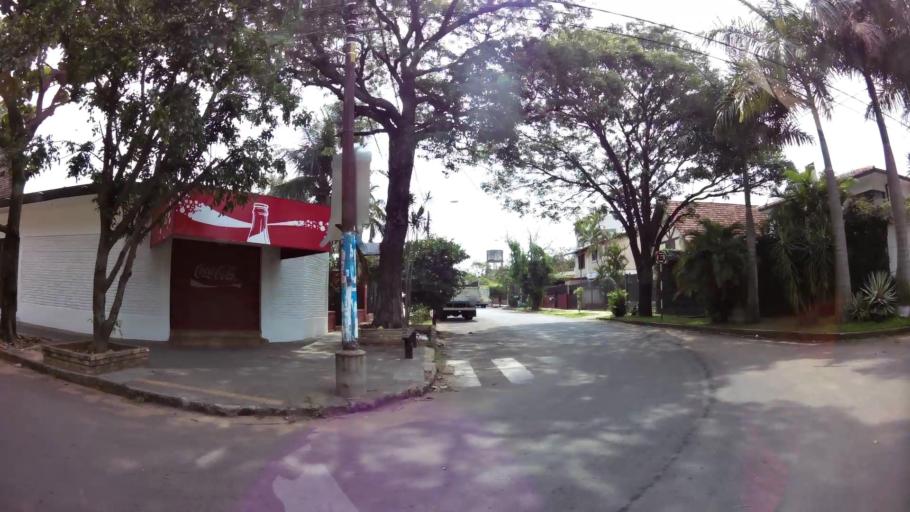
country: PY
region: Asuncion
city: Asuncion
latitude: -25.2802
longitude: -57.5690
